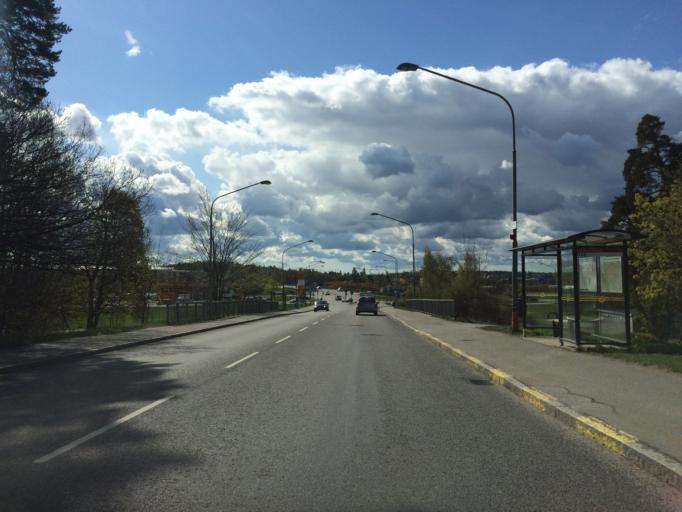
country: SE
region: Stockholm
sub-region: Huddinge Kommun
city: Segeltorp
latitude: 59.2913
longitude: 17.9465
